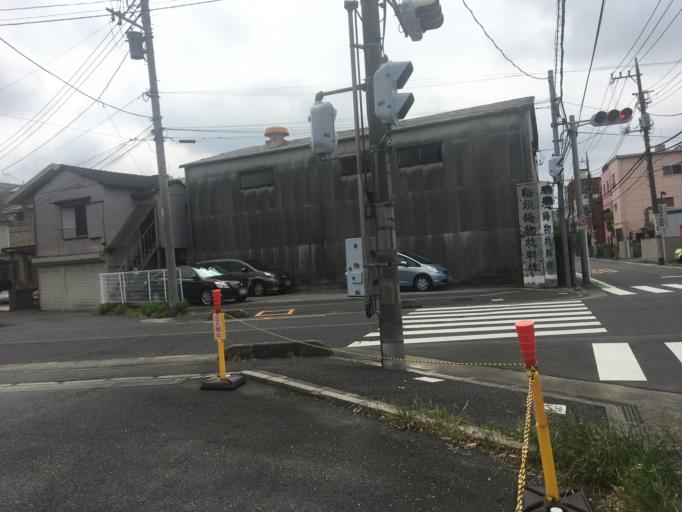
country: JP
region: Saitama
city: Kawaguchi
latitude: 35.8104
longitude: 139.7173
